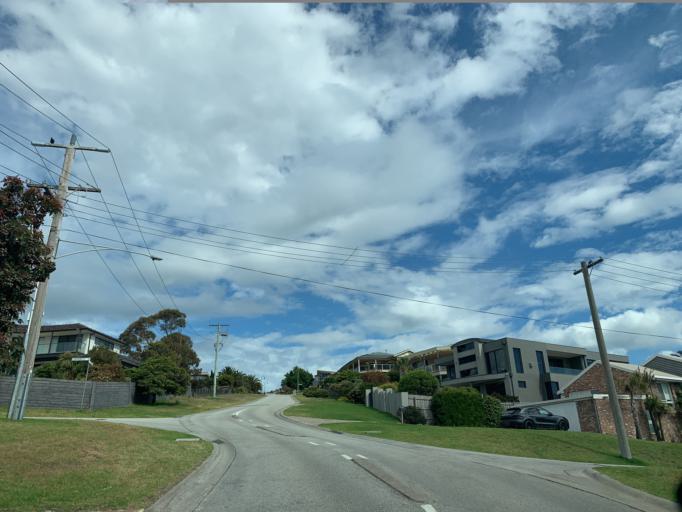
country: AU
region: Victoria
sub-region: Mornington Peninsula
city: Mount Martha
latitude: -38.2855
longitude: 144.9940
